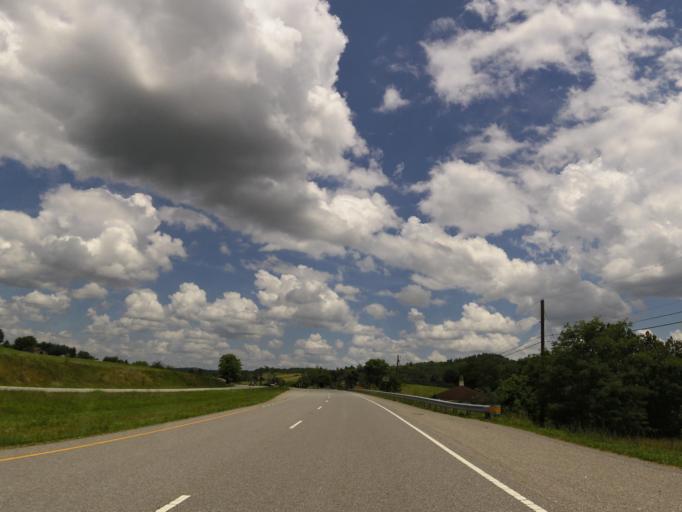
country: US
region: Tennessee
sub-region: Claiborne County
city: Harrogate
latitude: 36.6289
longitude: -83.4693
